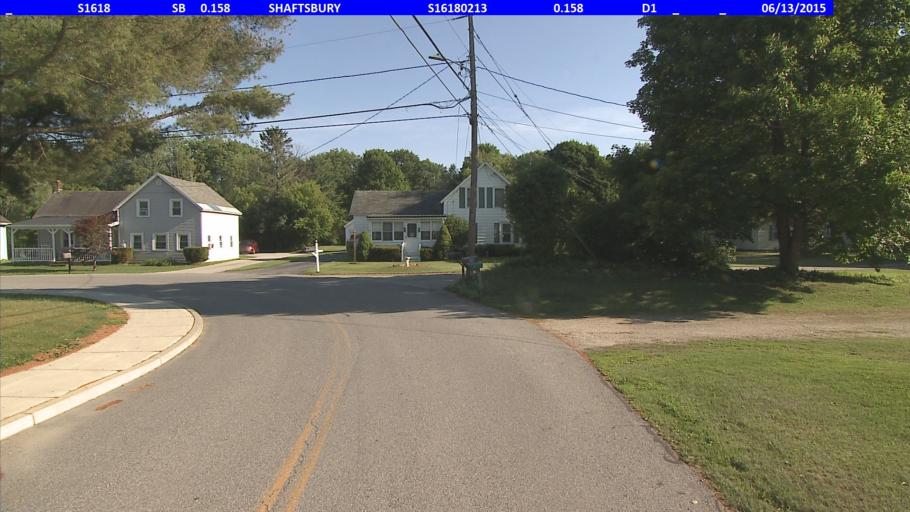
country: US
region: Vermont
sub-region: Bennington County
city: North Bennington
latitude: 42.9416
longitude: -73.2127
